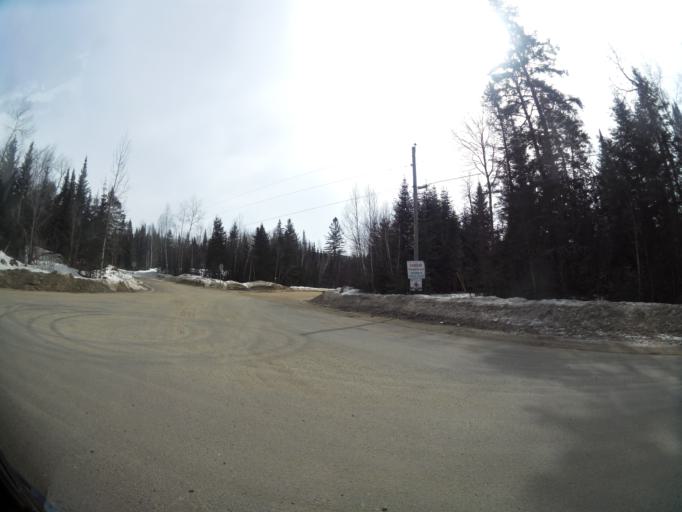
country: CA
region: Quebec
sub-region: Outaouais
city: Val-des-Monts
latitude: 45.9699
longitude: -75.5383
